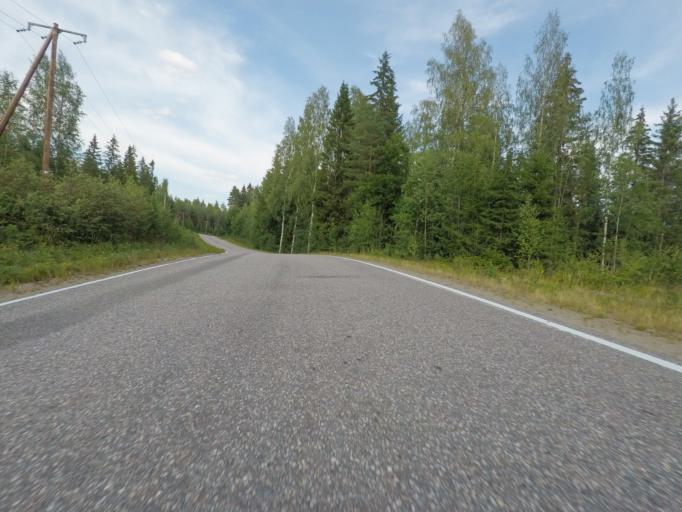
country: FI
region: Southern Savonia
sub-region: Savonlinna
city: Sulkava
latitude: 61.7521
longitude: 28.2144
